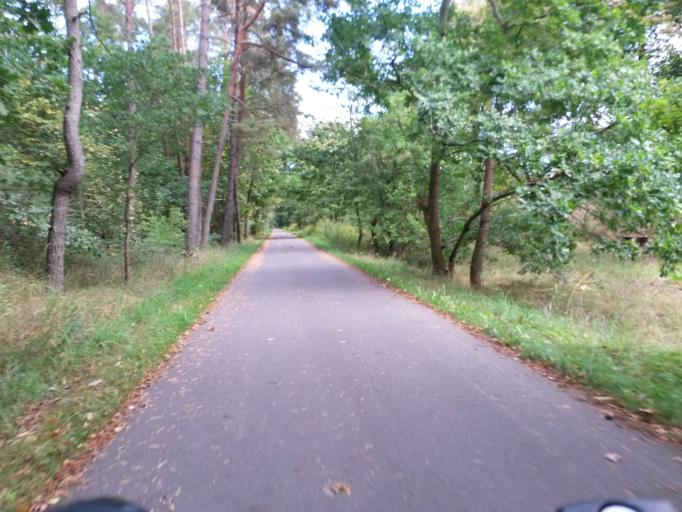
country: DE
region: Brandenburg
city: Templin
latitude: 53.1818
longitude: 13.5132
